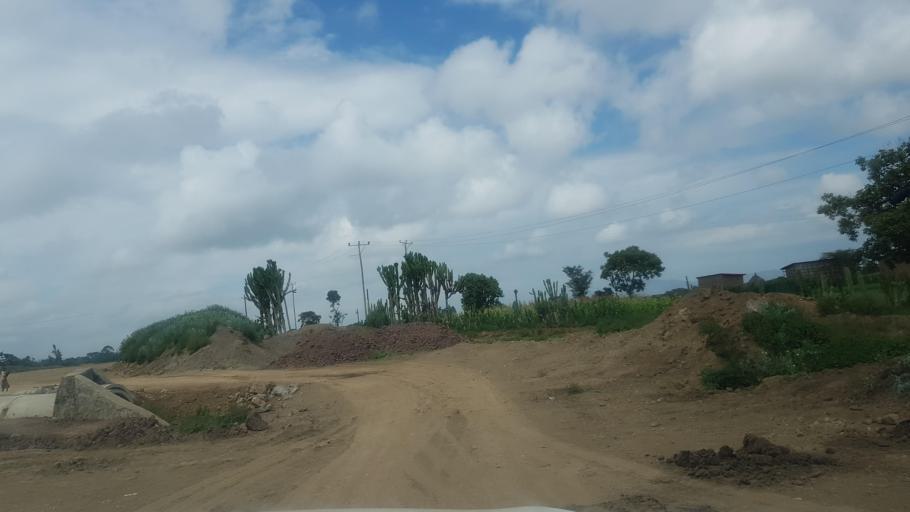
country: ET
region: Oromiya
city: Shashemene
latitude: 7.2559
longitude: 38.5936
